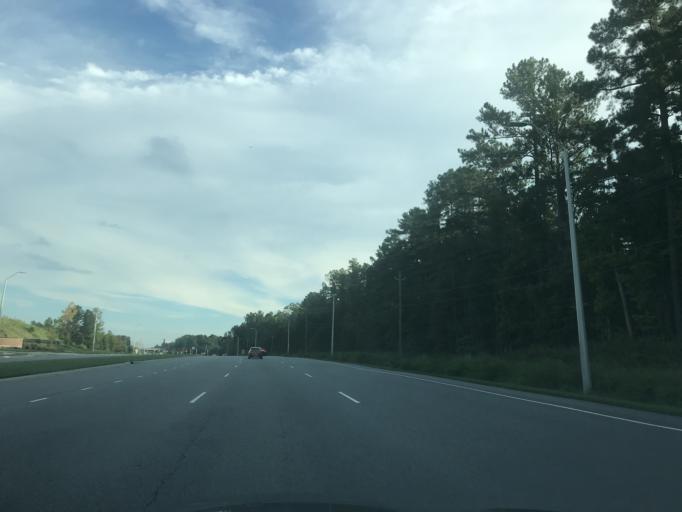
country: US
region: North Carolina
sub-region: Wake County
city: Green Level
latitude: 35.8499
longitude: -78.8938
